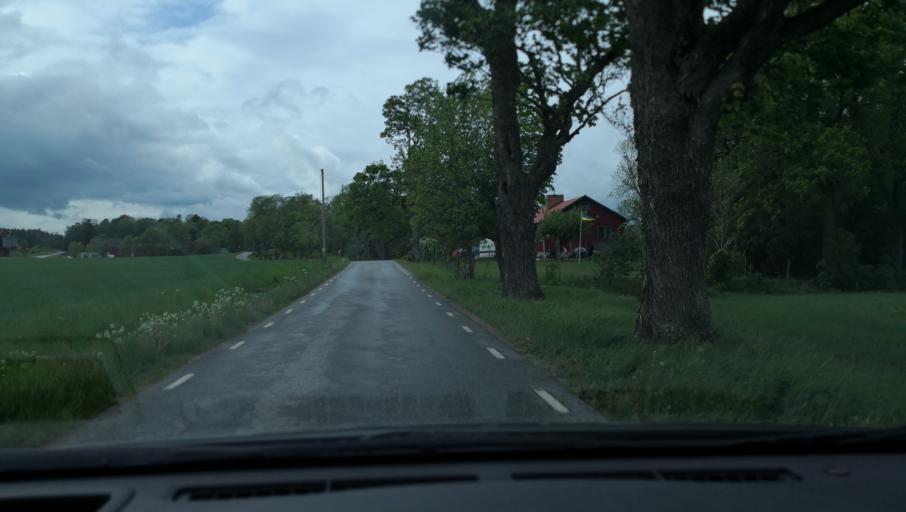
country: SE
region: Uppsala
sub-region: Enkopings Kommun
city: Orsundsbro
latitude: 59.7237
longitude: 17.4005
